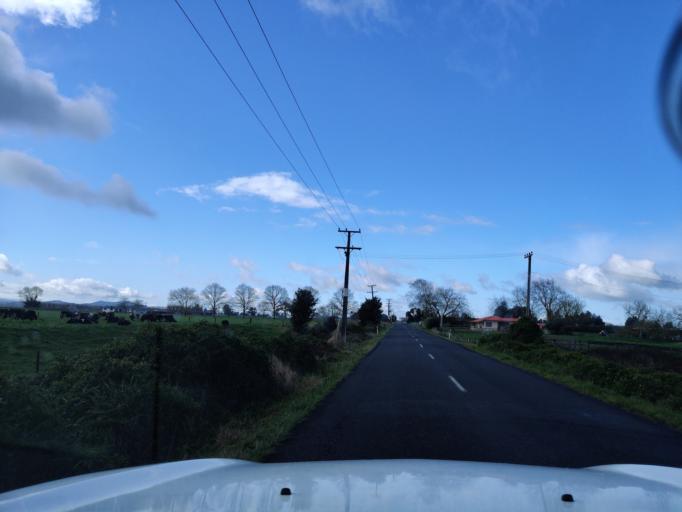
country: NZ
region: Waikato
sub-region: Waikato District
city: Ngaruawahia
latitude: -37.5772
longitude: 175.2703
